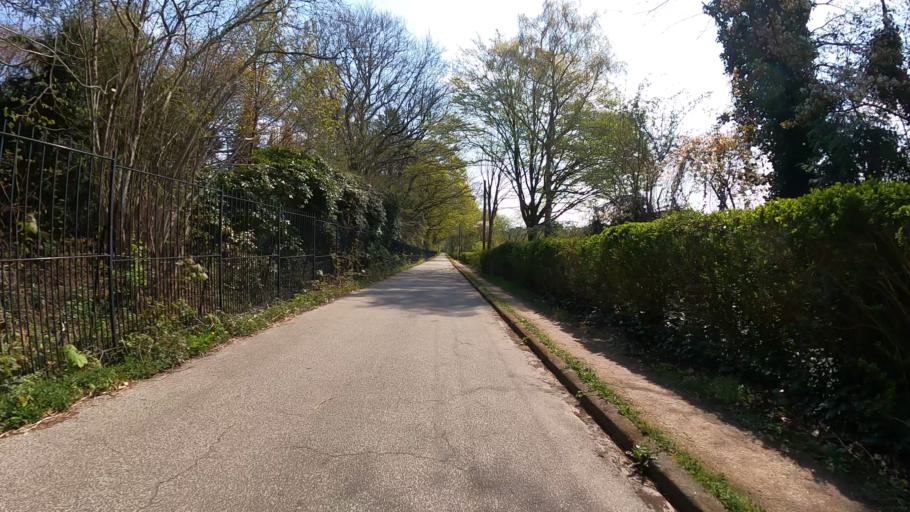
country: DE
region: Hamburg
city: Steilshoop
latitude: 53.6183
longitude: 10.0518
